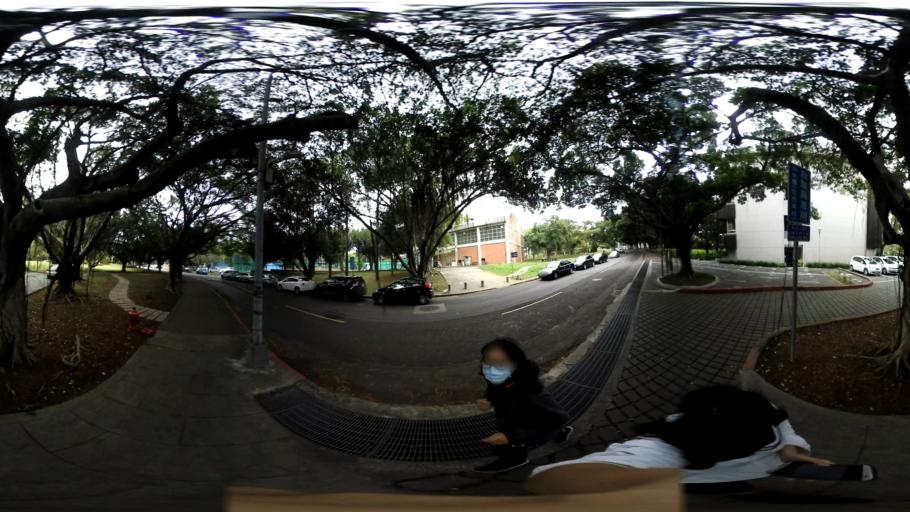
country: TW
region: Taiwan
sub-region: Hsinchu
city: Hsinchu
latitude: 24.7875
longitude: 121.0011
